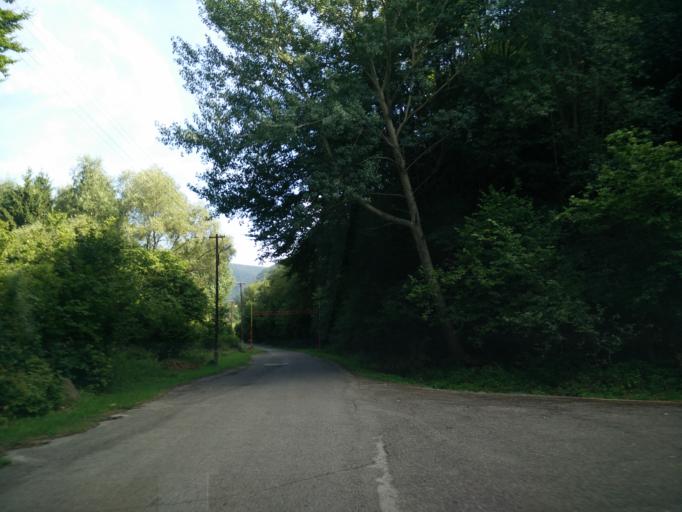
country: SK
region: Nitriansky
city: Novaky
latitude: 48.6618
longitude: 18.6312
